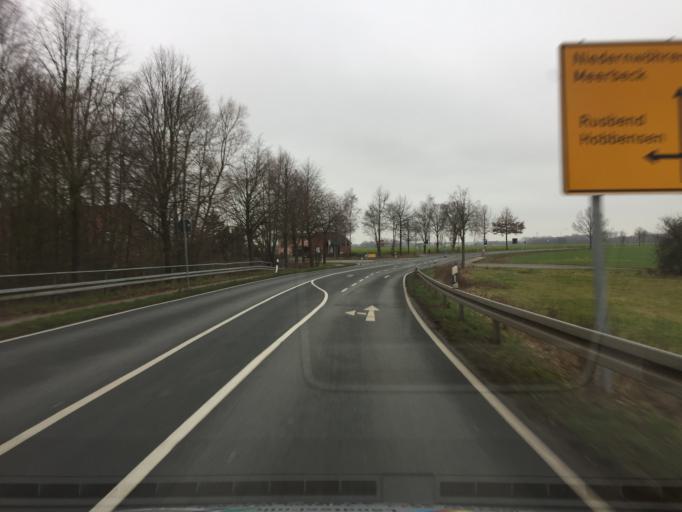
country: DE
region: Lower Saxony
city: Meerbeck
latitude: 52.3243
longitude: 9.1479
